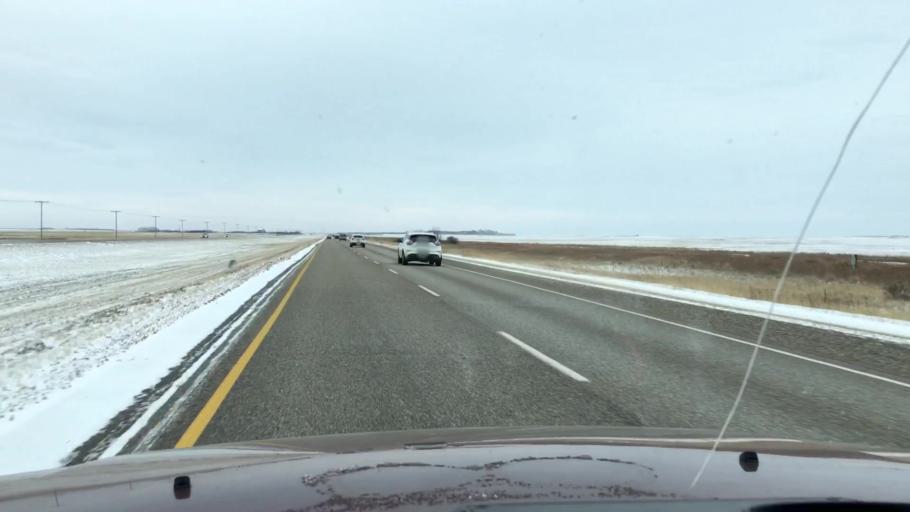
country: CA
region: Saskatchewan
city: Moose Jaw
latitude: 50.9960
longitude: -105.7590
